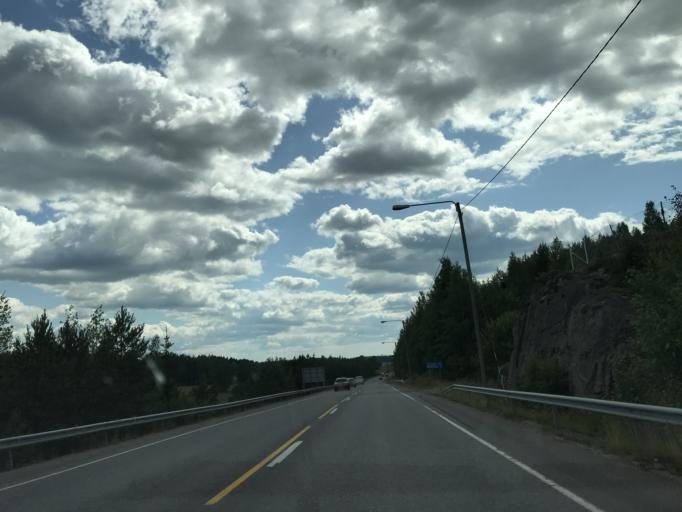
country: FI
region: Uusimaa
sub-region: Helsinki
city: Maentsaelae
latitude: 60.6677
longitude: 25.3502
